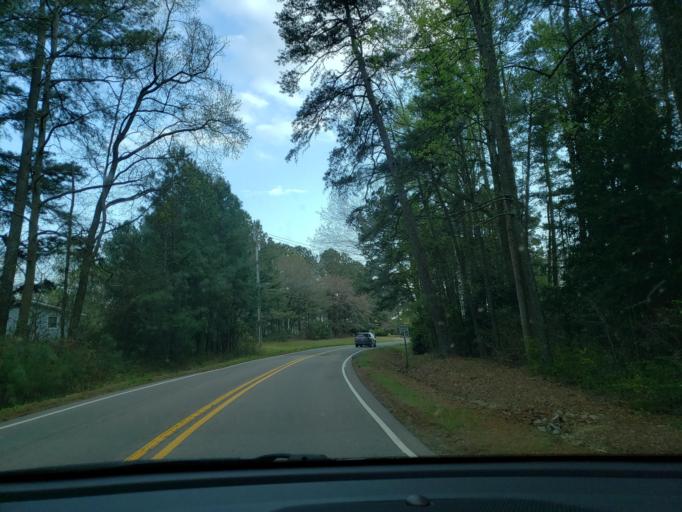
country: US
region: North Carolina
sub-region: Wake County
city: Green Level
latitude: 35.7536
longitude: -78.8947
